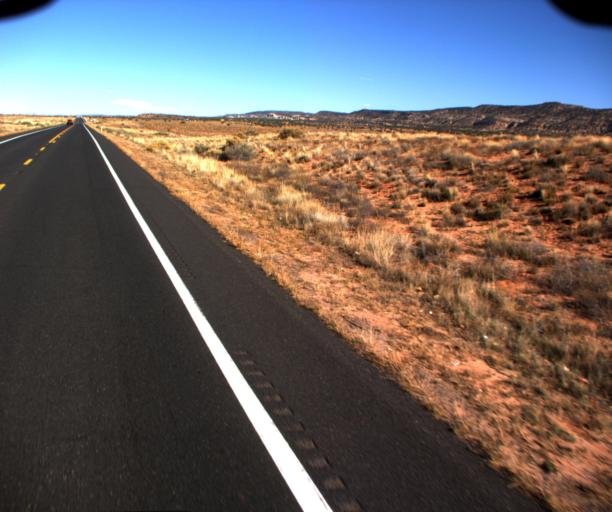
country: US
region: Arizona
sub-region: Coconino County
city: Kaibito
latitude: 36.3955
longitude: -110.8692
